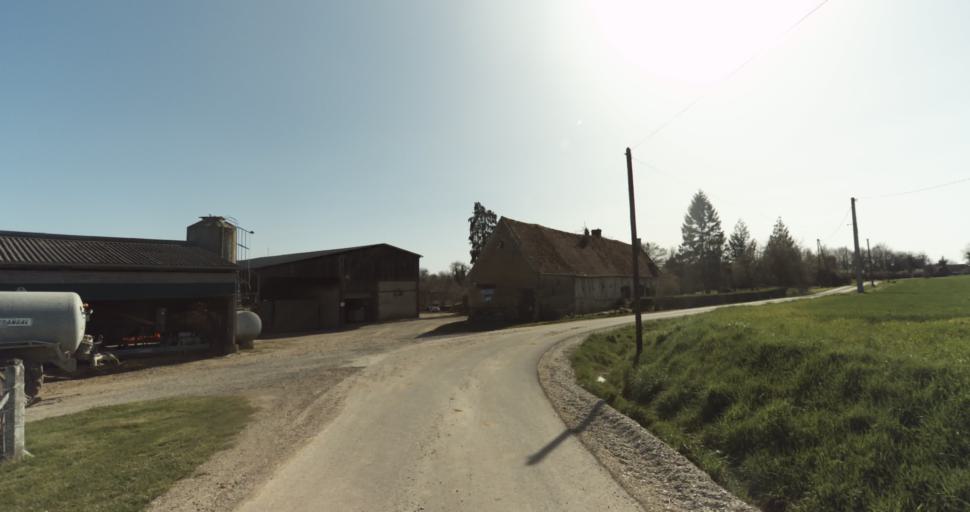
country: FR
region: Lower Normandy
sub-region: Departement du Calvados
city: Saint-Pierre-sur-Dives
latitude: 48.9375
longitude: 0.0081
